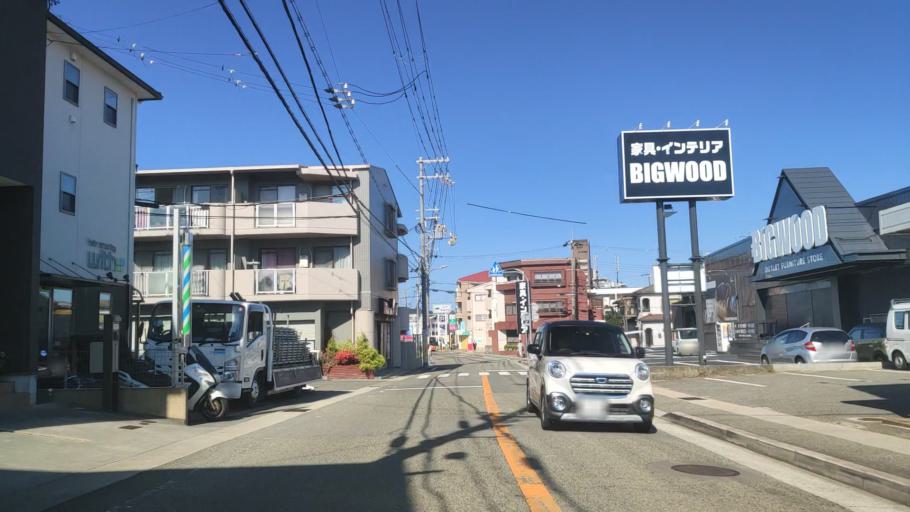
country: JP
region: Hyogo
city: Akashi
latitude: 34.6608
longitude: 135.0178
